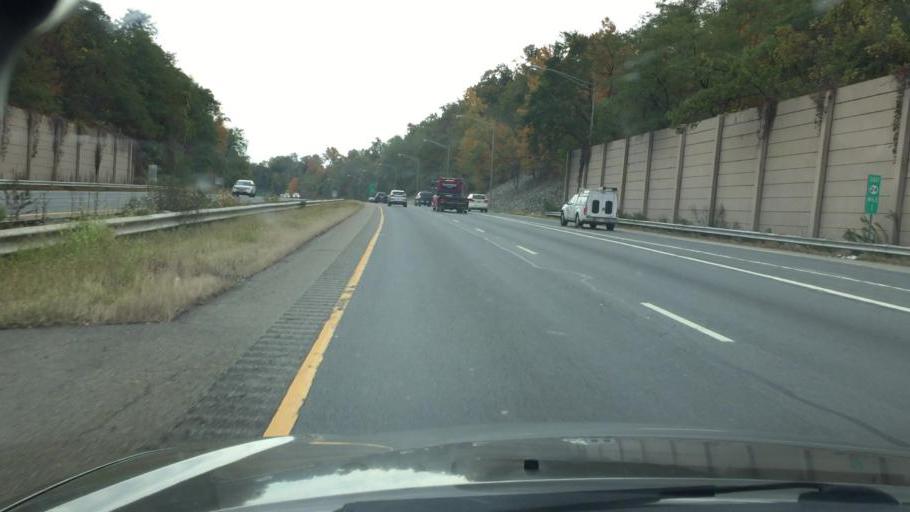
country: US
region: New Jersey
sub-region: Morris County
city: Morristown
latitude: 40.8025
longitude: -74.4432
